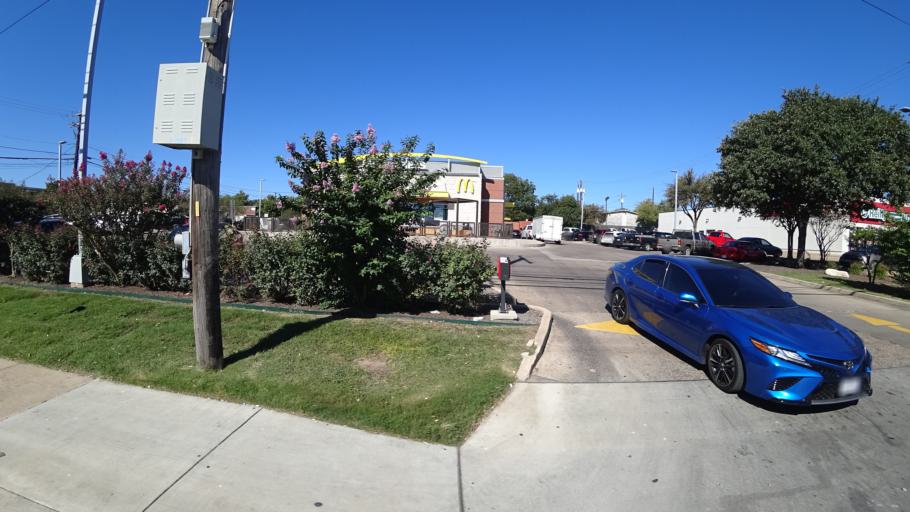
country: US
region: Texas
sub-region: Travis County
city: Austin
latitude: 30.3236
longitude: -97.7279
